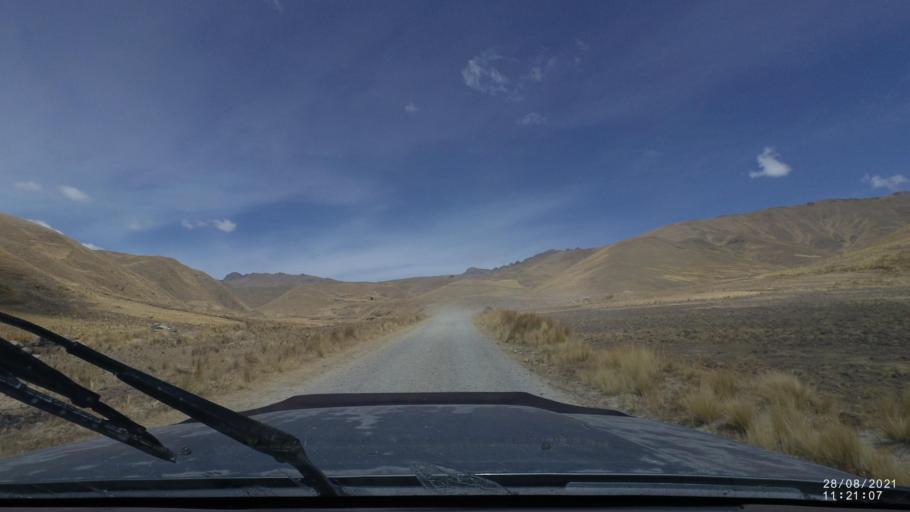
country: BO
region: Cochabamba
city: Sipe Sipe
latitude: -17.1633
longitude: -66.3450
